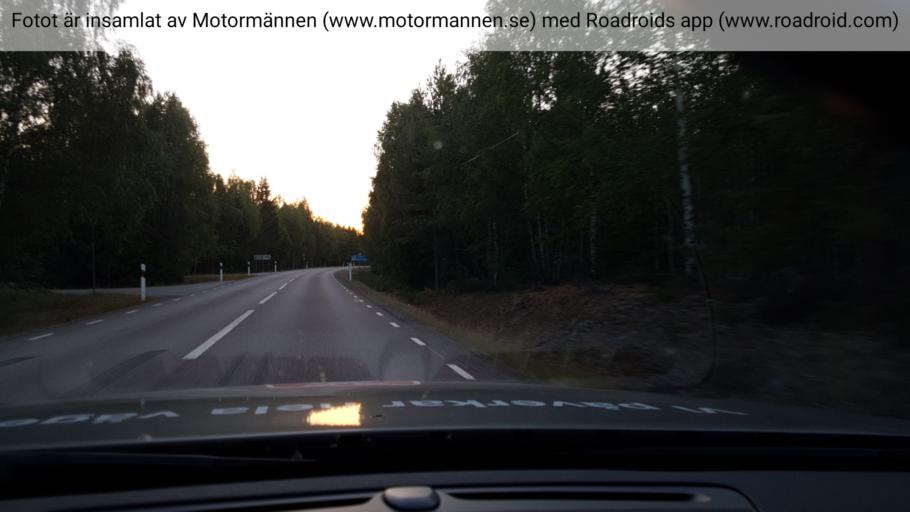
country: SE
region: Uppsala
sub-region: Heby Kommun
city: OEstervala
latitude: 60.0388
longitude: 17.2483
